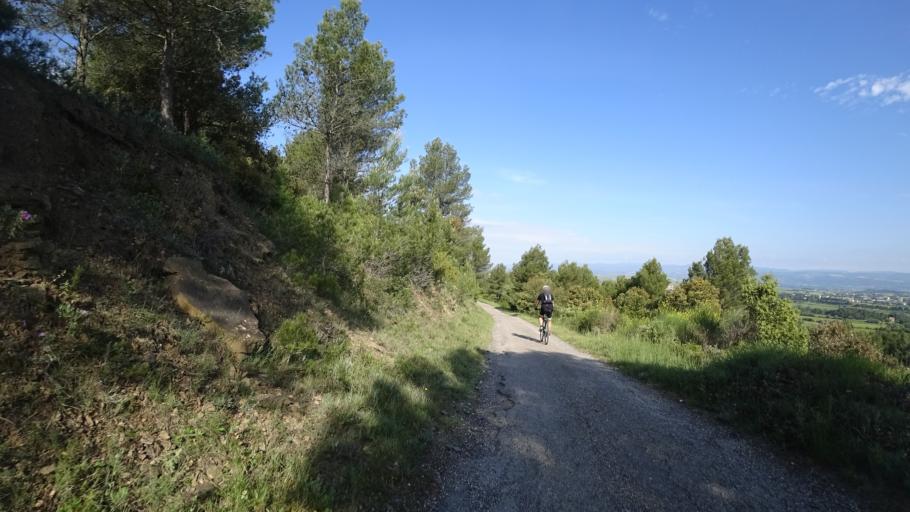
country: FR
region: Languedoc-Roussillon
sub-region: Departement de l'Herault
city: Olonzac
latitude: 43.2527
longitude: 2.7394
